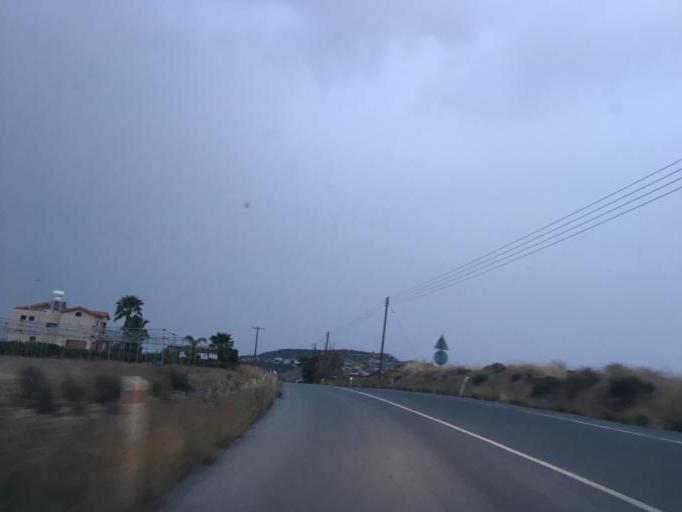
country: CY
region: Limassol
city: Parekklisha
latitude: 34.7561
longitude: 33.1600
